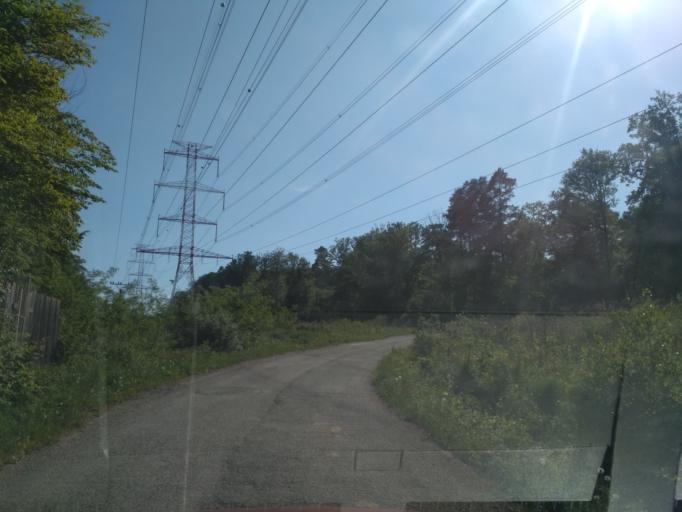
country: SK
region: Kosicky
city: Kosice
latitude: 48.7315
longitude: 21.1854
